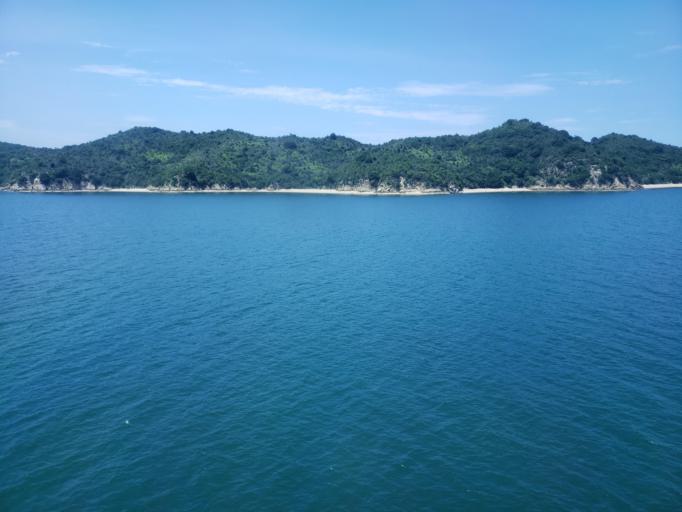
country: JP
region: Kagawa
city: Takamatsu-shi
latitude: 34.3977
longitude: 134.1091
